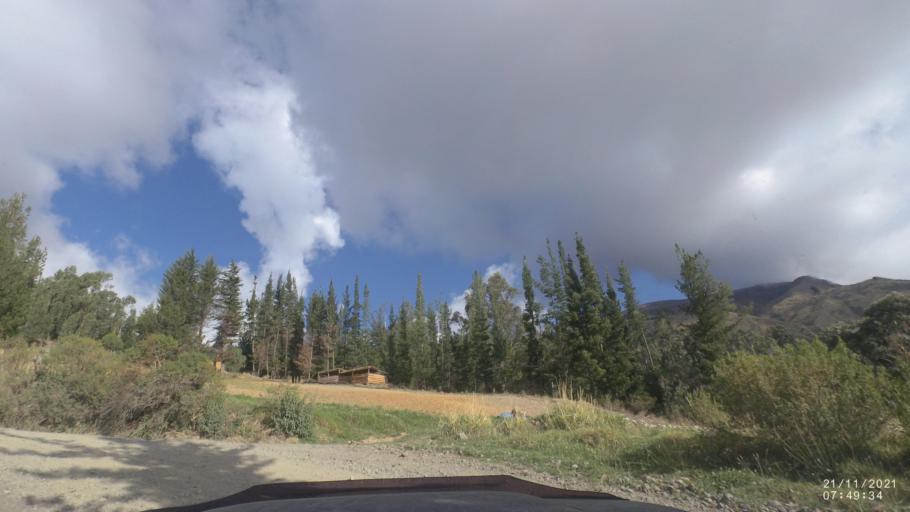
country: BO
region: Cochabamba
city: Cochabamba
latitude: -17.3088
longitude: -66.2134
